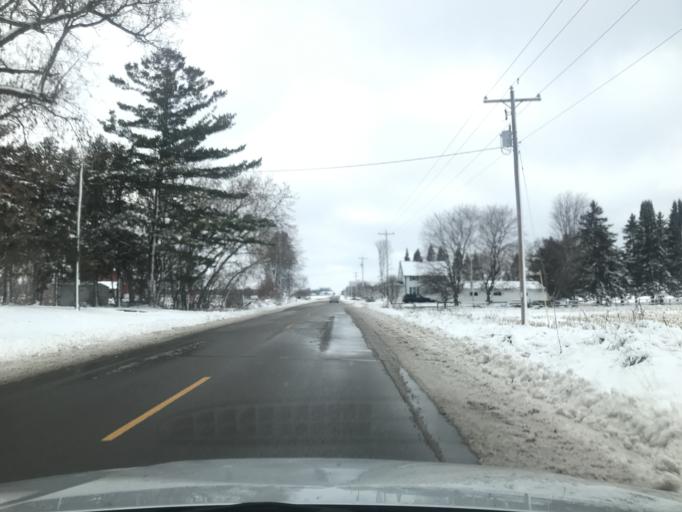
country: US
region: Wisconsin
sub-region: Oconto County
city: Oconto
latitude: 44.9500
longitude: -87.8923
